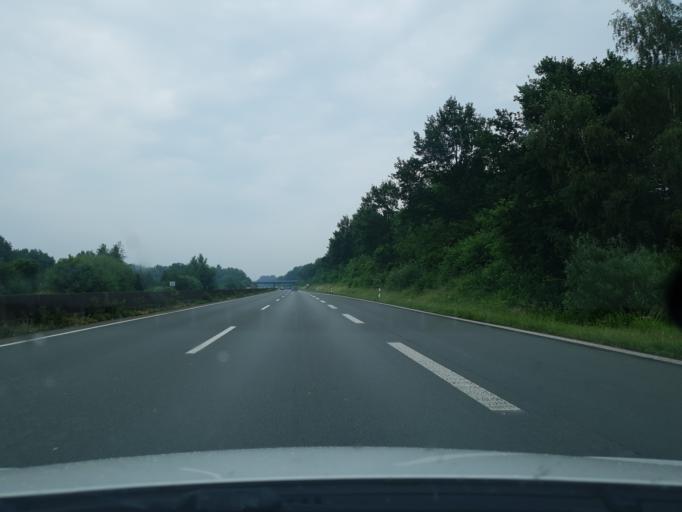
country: DE
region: North Rhine-Westphalia
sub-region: Regierungsbezirk Munster
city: Velen
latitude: 51.8931
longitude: 7.0217
